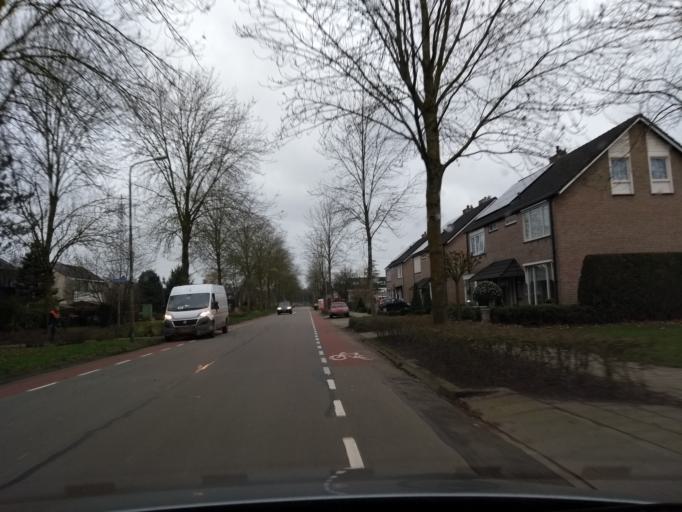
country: NL
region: Overijssel
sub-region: Gemeente Borne
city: Borne
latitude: 52.2934
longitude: 6.7405
